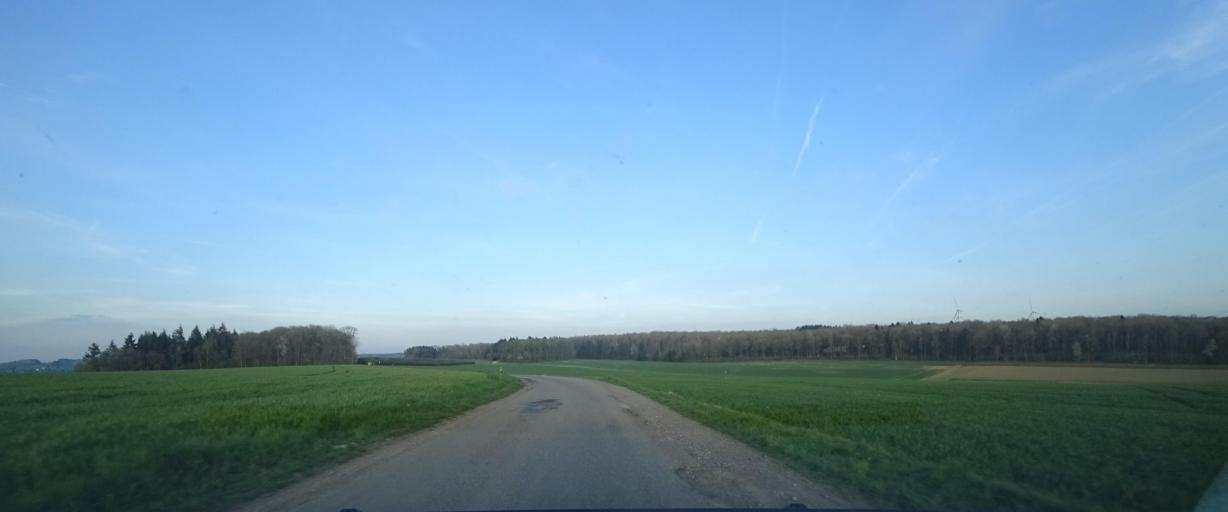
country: BE
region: Wallonia
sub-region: Province de Namur
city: Hamois
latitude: 50.3093
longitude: 5.1597
